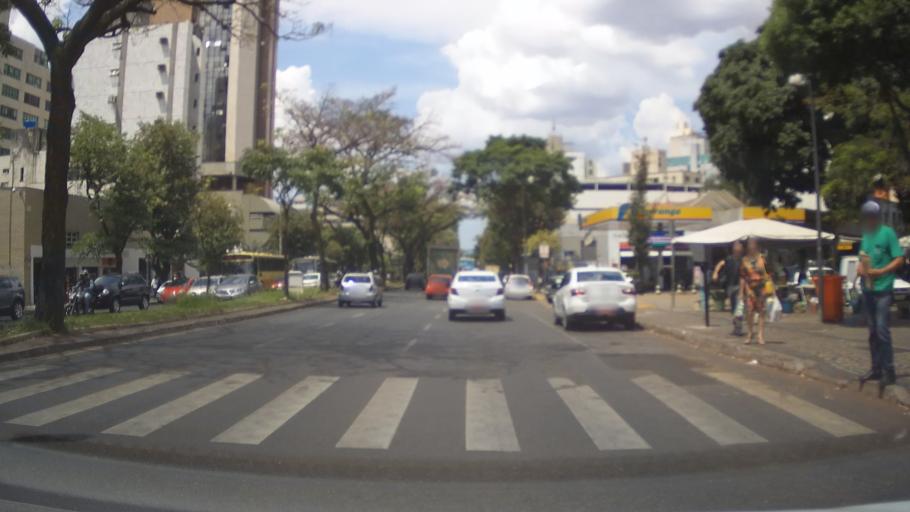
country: BR
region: Minas Gerais
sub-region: Belo Horizonte
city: Belo Horizonte
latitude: -19.9282
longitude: -43.9287
